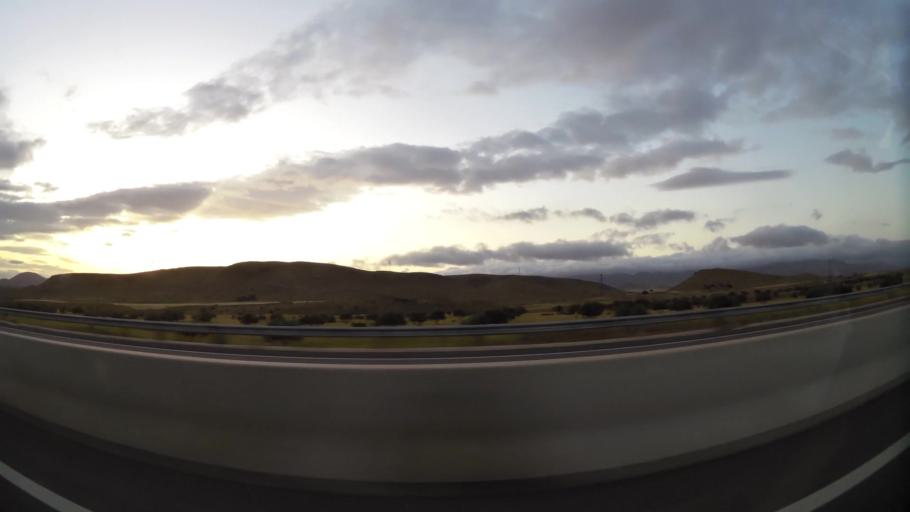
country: MA
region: Oriental
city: El Aioun
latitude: 34.6102
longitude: -2.5599
